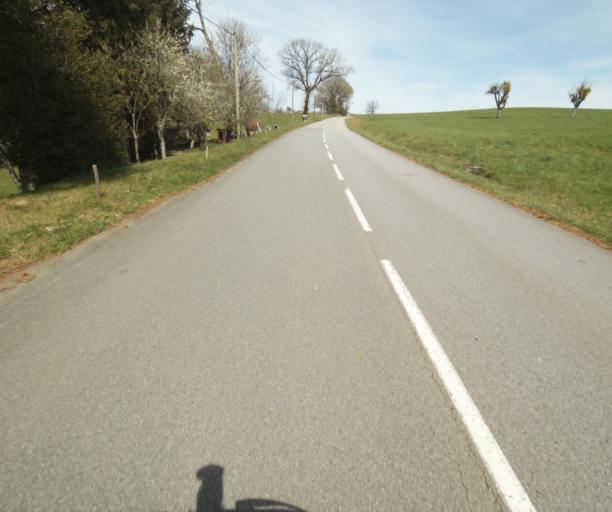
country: FR
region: Limousin
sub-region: Departement de la Correze
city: Correze
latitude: 45.3833
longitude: 1.8052
